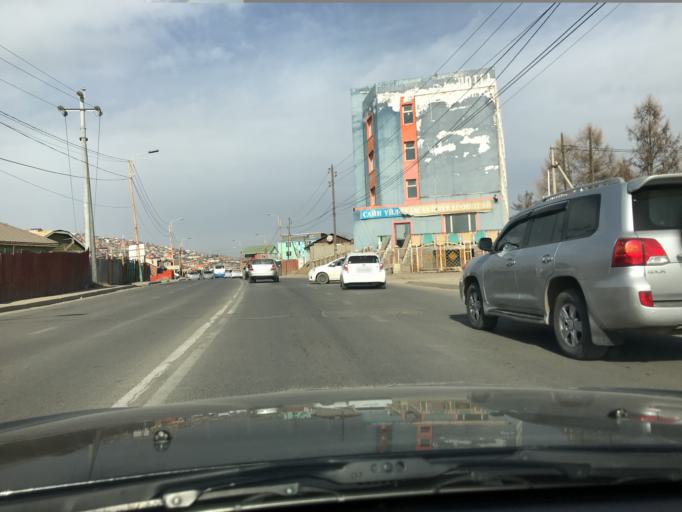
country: MN
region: Ulaanbaatar
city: Ulaanbaatar
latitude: 47.9337
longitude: 106.8866
